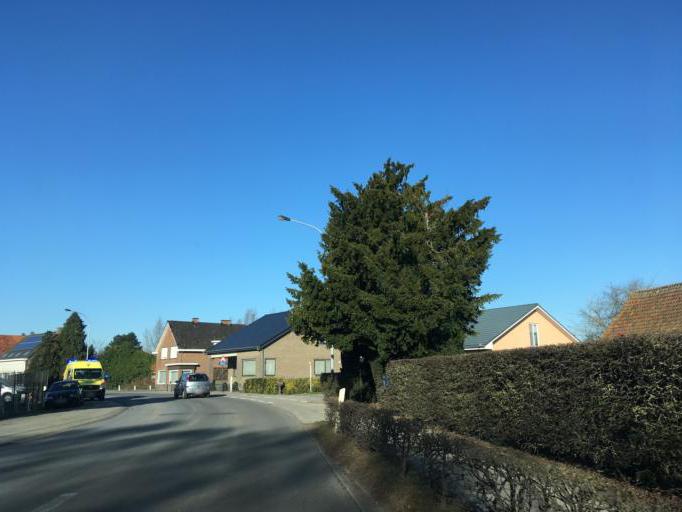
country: BE
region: Flanders
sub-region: Provincie Oost-Vlaanderen
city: Zomergem
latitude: 51.1162
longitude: 3.5758
